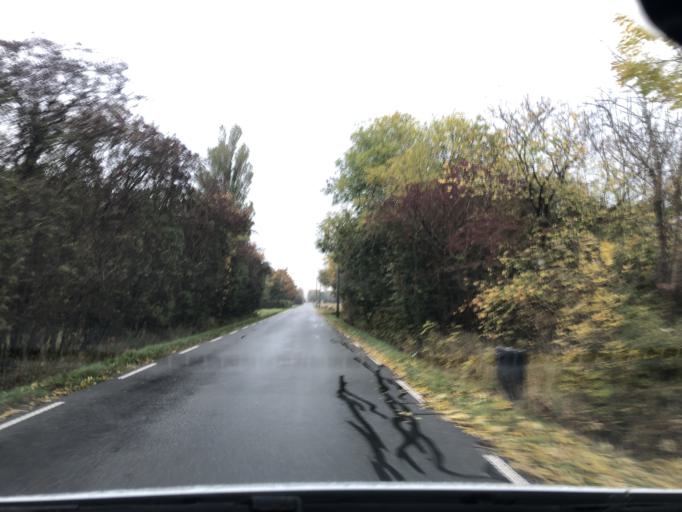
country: DK
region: Capital Region
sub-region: Tarnby Kommune
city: Tarnby
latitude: 55.5637
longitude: 12.5896
